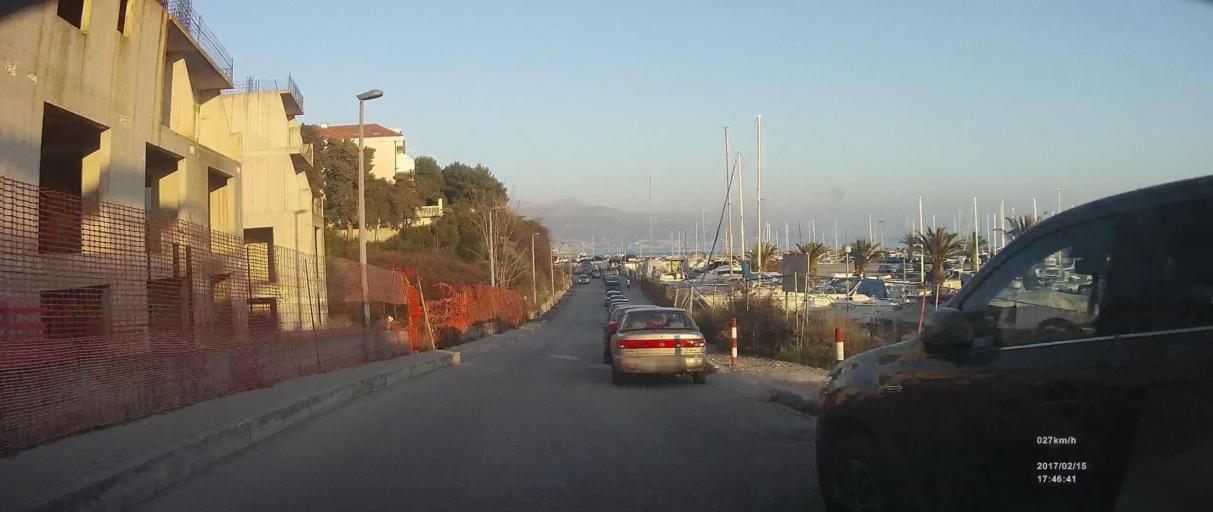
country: HR
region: Splitsko-Dalmatinska
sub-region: Grad Split
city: Split
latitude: 43.5010
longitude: 16.4590
